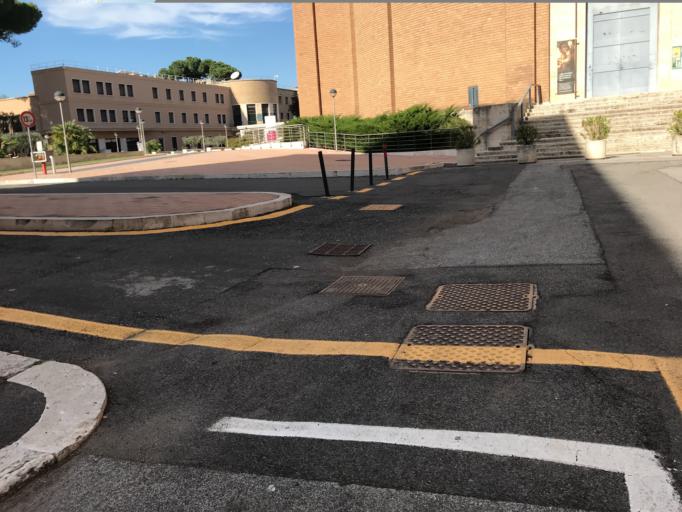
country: IT
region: Latium
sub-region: Citta metropolitana di Roma Capitale
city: Rome
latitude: 41.9031
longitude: 12.5127
